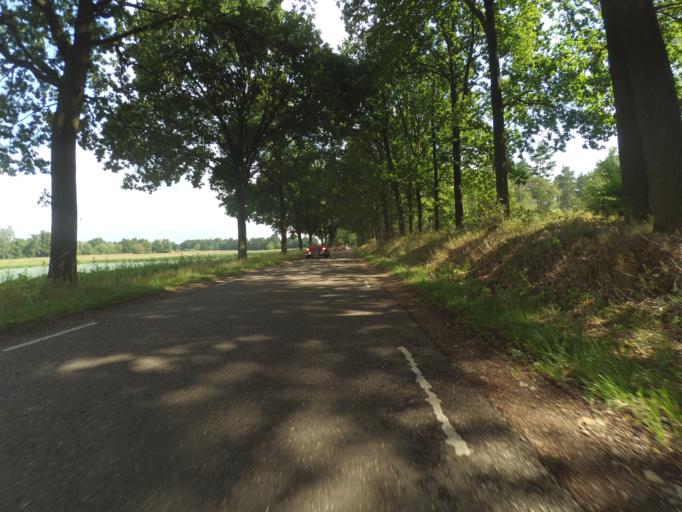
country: NL
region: Limburg
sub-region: Gemeente Echt-Susteren
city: Koningsbosch
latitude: 51.0811
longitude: 5.9272
